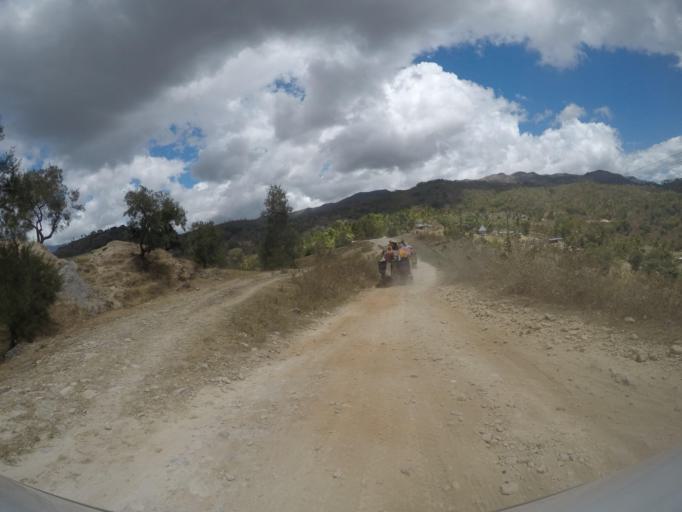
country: TL
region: Baucau
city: Baucau
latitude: -8.5029
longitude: 126.6795
